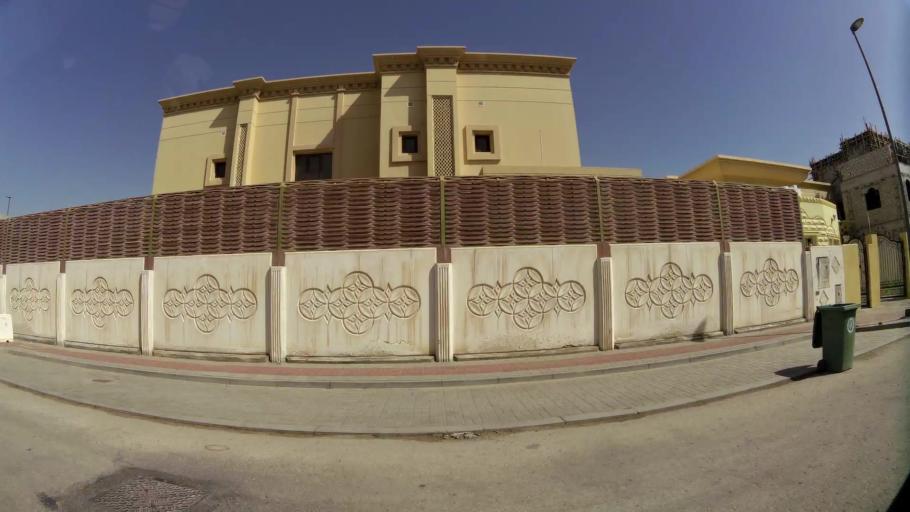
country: QA
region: Baladiyat ad Dawhah
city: Doha
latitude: 25.3605
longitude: 51.5006
